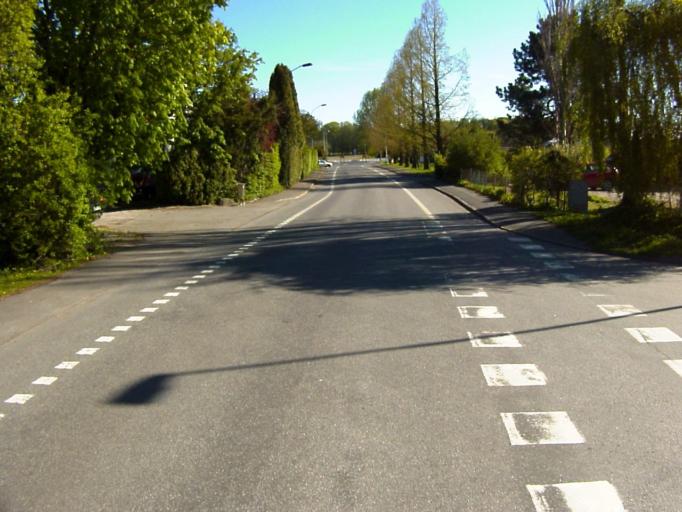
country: SE
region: Skane
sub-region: Kristianstads Kommun
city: Kristianstad
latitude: 56.0302
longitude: 14.1985
